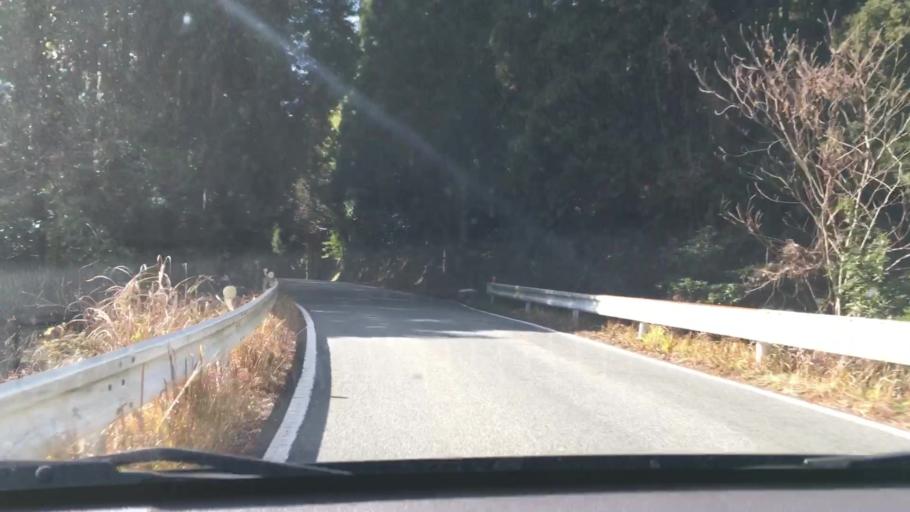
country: JP
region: Kagoshima
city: Ijuin
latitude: 31.7154
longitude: 130.4151
